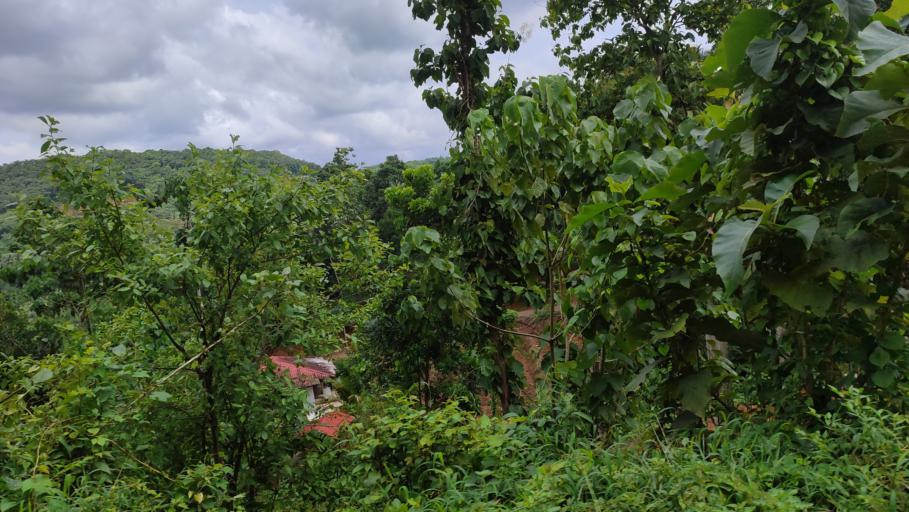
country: IN
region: Kerala
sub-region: Kasaragod District
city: Nileshwar
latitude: 12.2953
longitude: 75.2866
